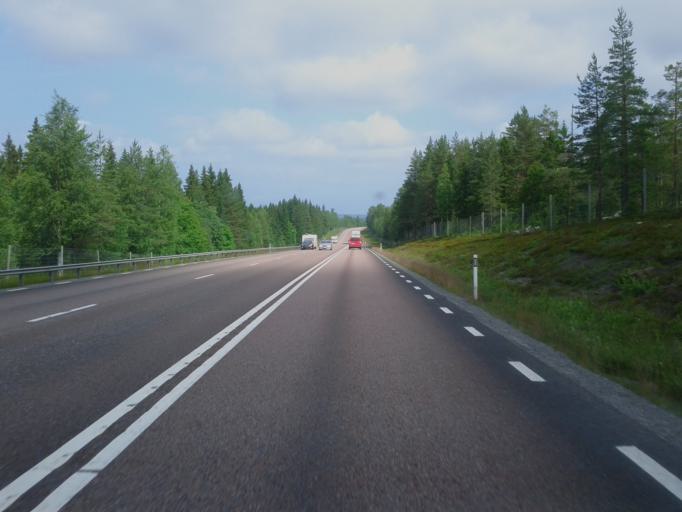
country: SE
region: Vaesterbotten
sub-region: Skelleftea Kommun
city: Burea
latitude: 64.4458
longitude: 21.2833
